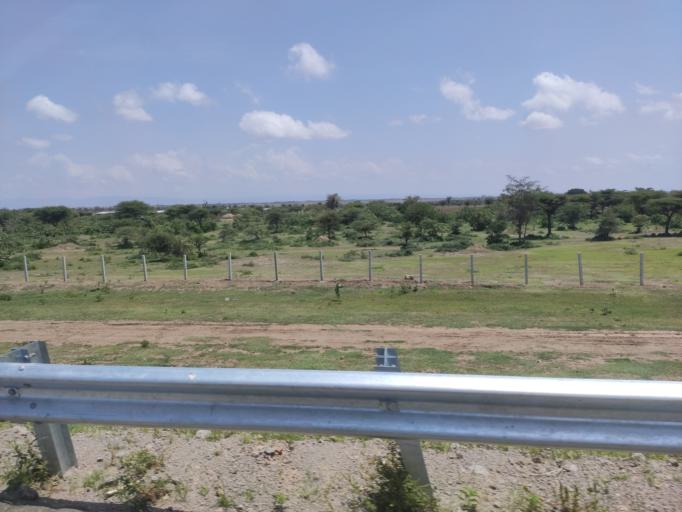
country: ET
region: Oromiya
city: Ziway
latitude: 8.2600
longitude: 38.8988
